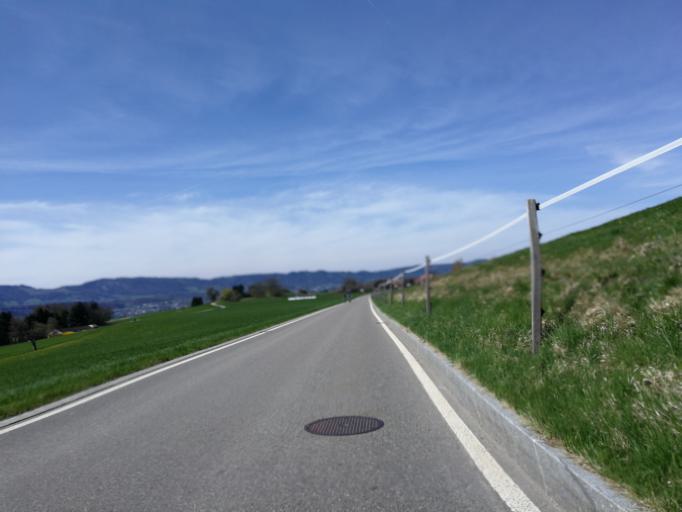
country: CH
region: Zurich
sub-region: Bezirk Meilen
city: Meilen
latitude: 47.2918
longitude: 8.6395
